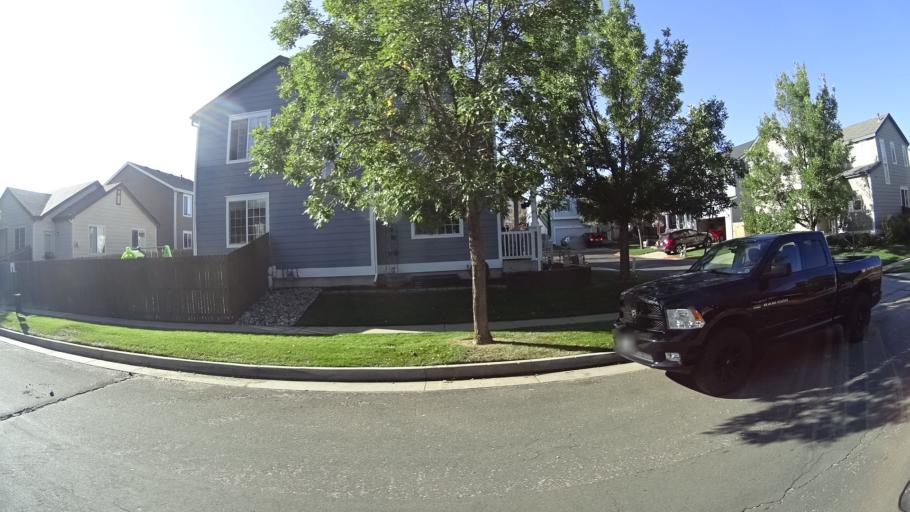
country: US
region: Colorado
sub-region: El Paso County
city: Cimarron Hills
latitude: 38.8760
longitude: -104.6967
